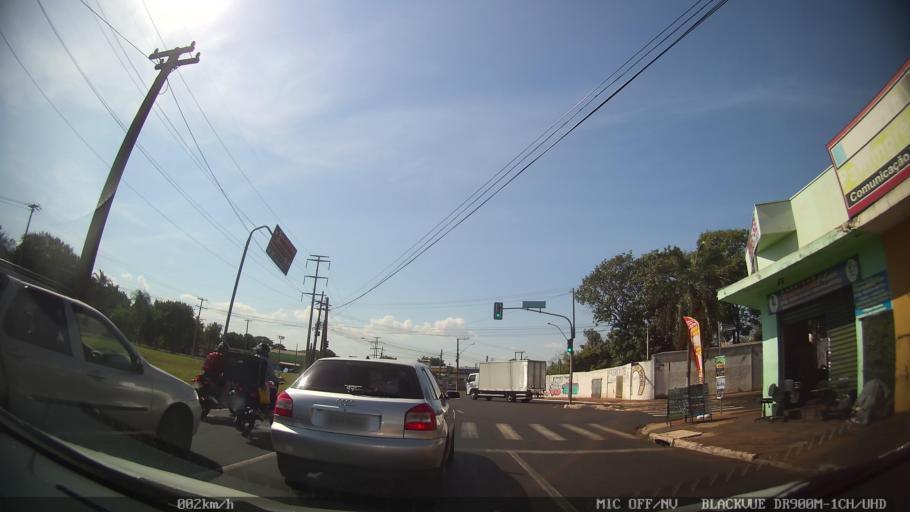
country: BR
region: Sao Paulo
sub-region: Ribeirao Preto
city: Ribeirao Preto
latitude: -21.1786
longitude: -47.8227
